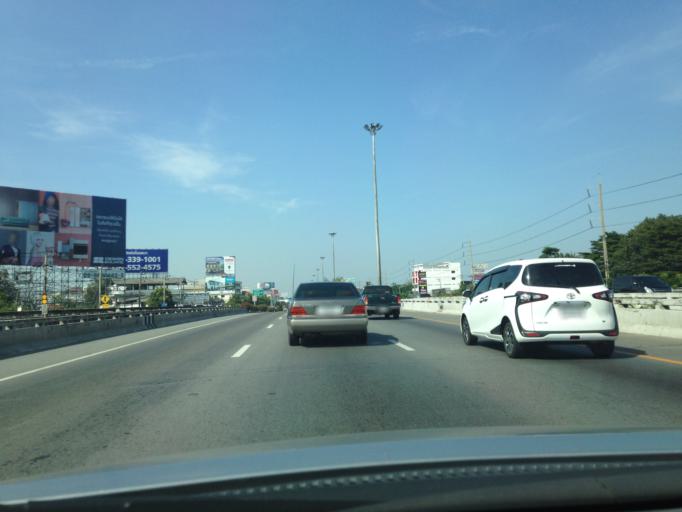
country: TH
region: Nonthaburi
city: Bang Yai
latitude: 13.8398
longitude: 100.4129
